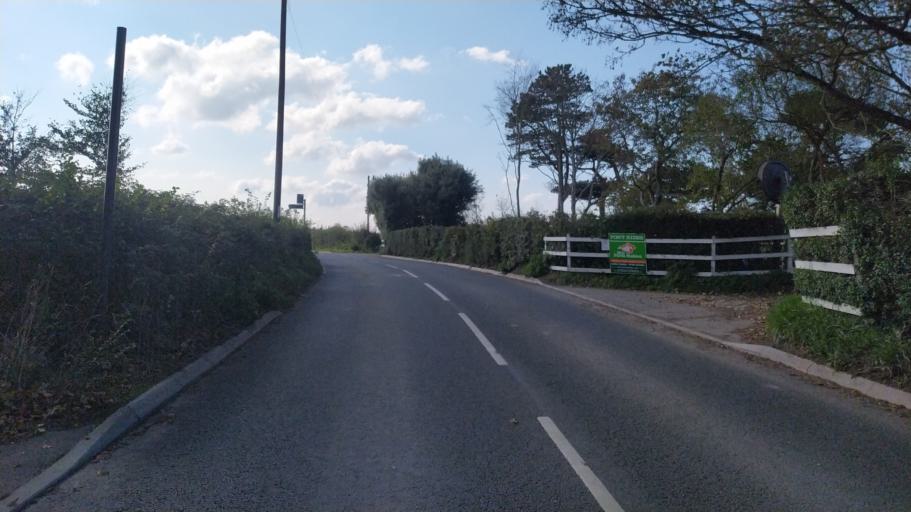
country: GB
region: England
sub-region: Isle of Wight
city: Freshwater
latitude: 50.6951
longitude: -1.5220
